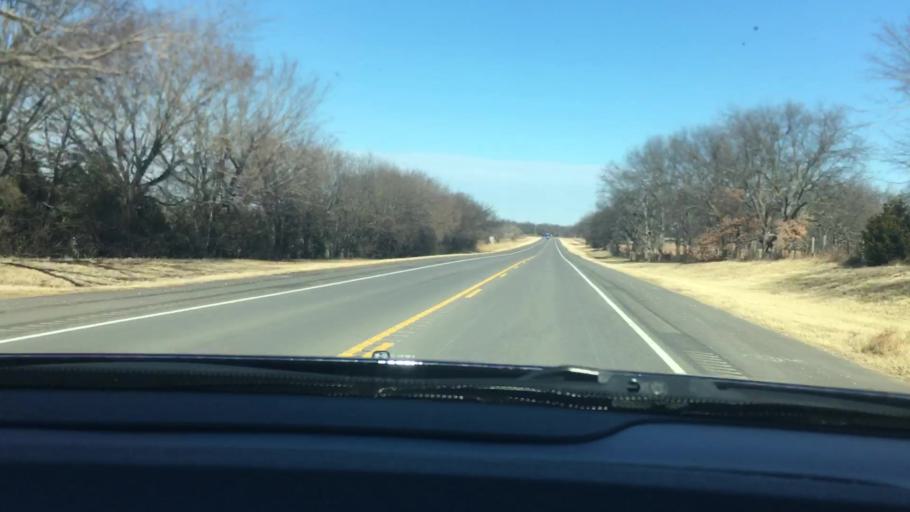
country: US
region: Oklahoma
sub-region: Murray County
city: Davis
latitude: 34.5214
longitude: -97.1205
